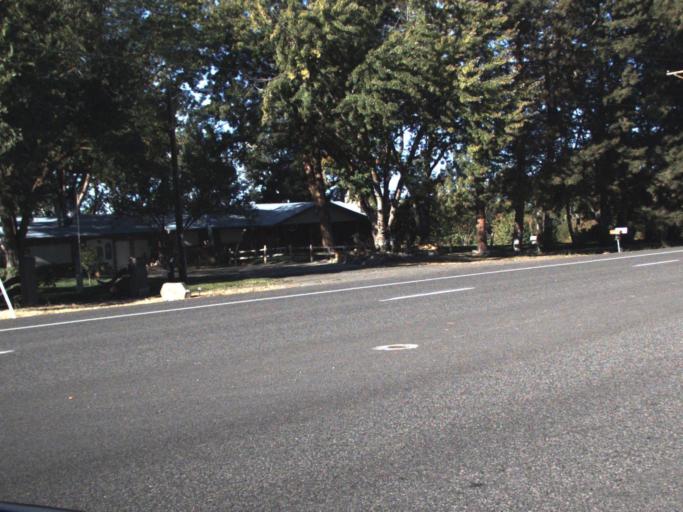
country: US
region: Washington
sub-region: Benton County
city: Richland
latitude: 46.2940
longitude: -119.3218
